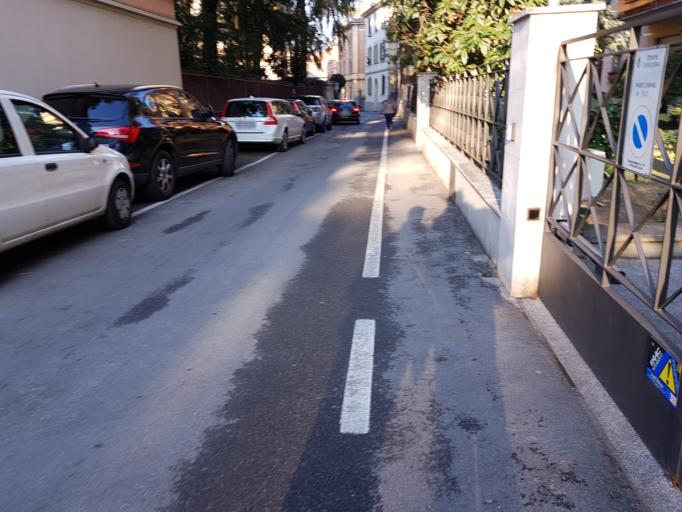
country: IT
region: Emilia-Romagna
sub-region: Provincia di Bologna
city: Bologna
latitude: 44.4846
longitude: 11.3584
